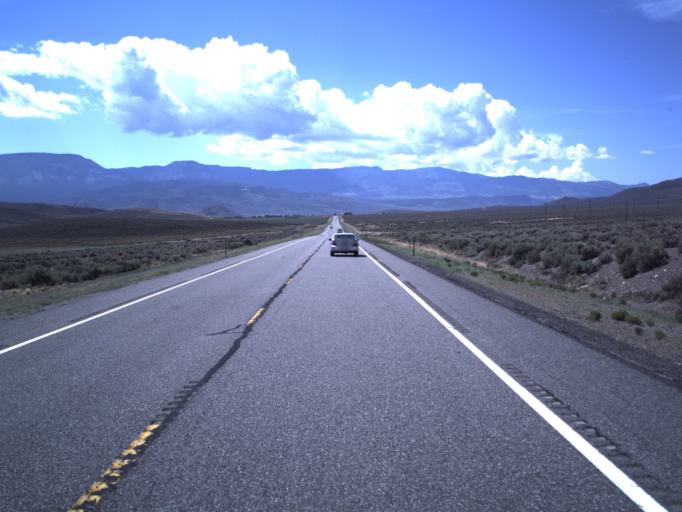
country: US
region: Utah
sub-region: Piute County
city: Junction
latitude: 38.2816
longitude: -112.2245
